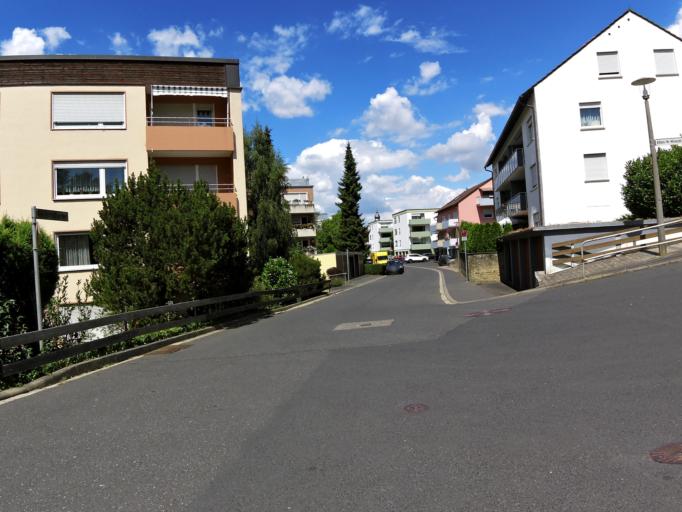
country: DE
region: Bavaria
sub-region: Regierungsbezirk Unterfranken
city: Estenfeld
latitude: 49.8073
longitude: 9.9847
